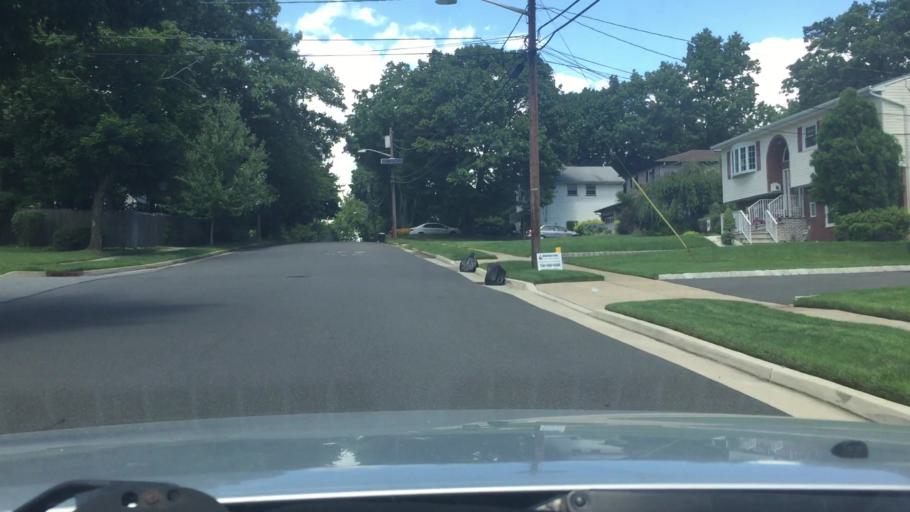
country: US
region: New Jersey
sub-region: Middlesex County
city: Old Bridge
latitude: 40.4174
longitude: -74.3783
